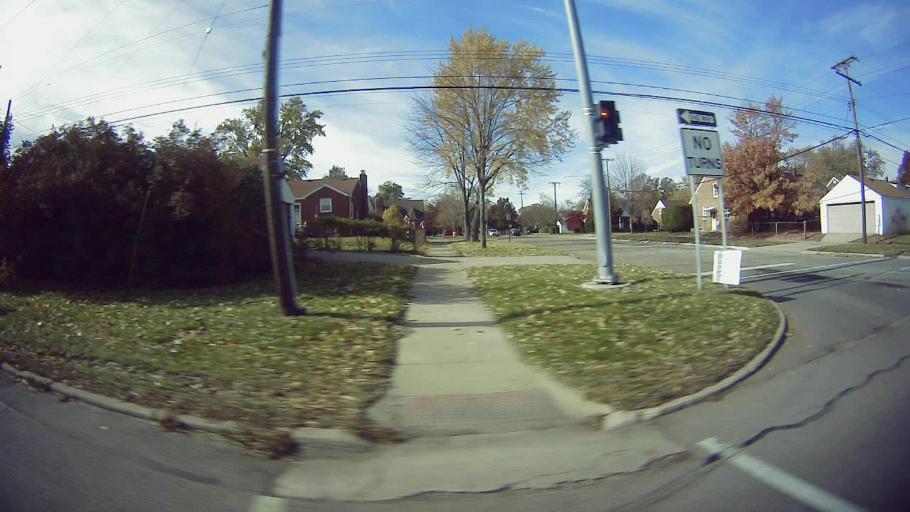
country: US
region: Michigan
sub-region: Wayne County
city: Dearborn Heights
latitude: 42.3197
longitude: -83.2725
